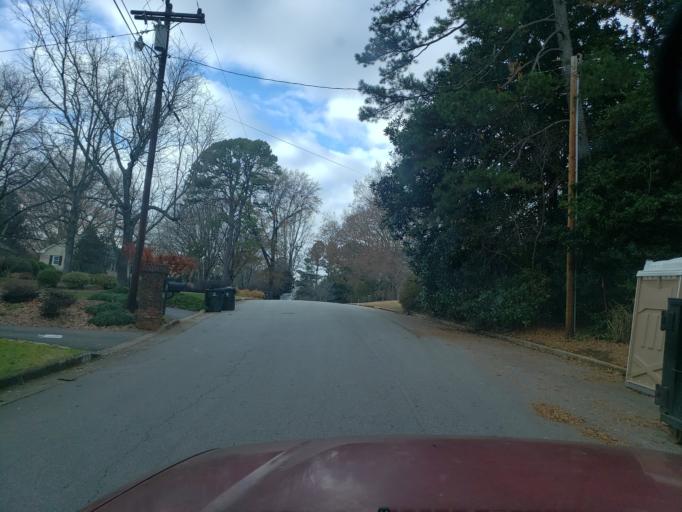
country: US
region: South Carolina
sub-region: Greenville County
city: Greenville
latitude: 34.8075
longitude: -82.3640
